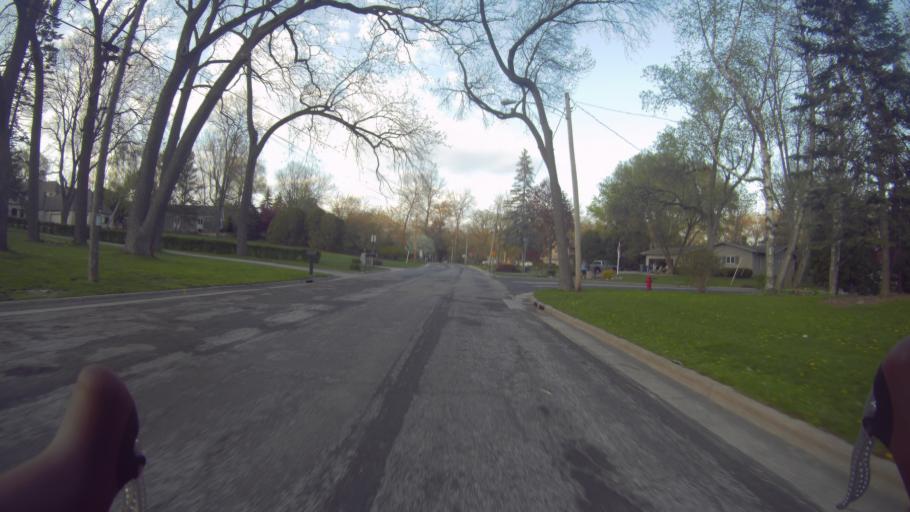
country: US
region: Wisconsin
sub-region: Dane County
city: Monona
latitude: 43.0645
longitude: -89.3477
